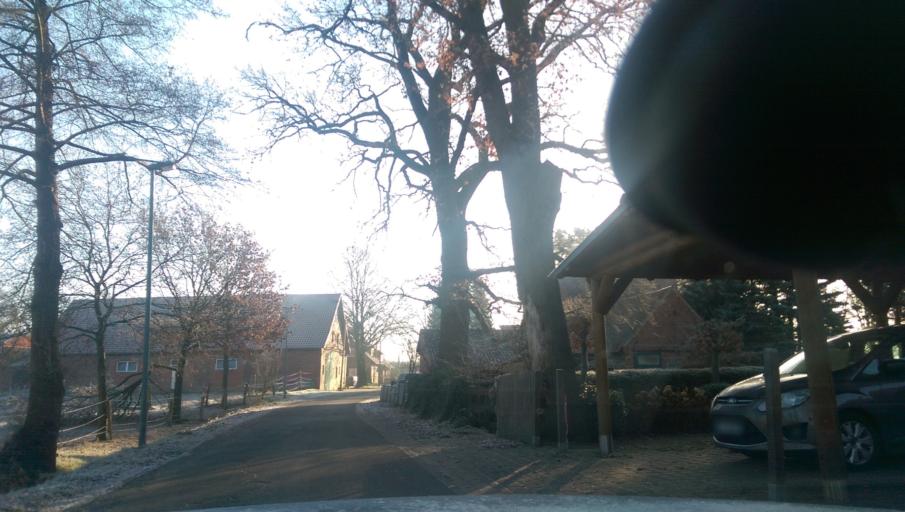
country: DE
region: Lower Saxony
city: Lindwedel
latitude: 52.5514
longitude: 9.6833
